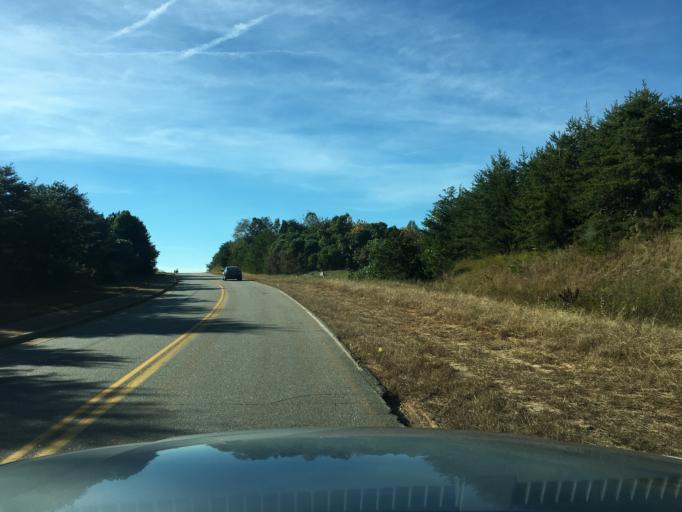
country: US
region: North Carolina
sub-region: Catawba County
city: Saint Stephens
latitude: 35.7041
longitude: -81.2799
